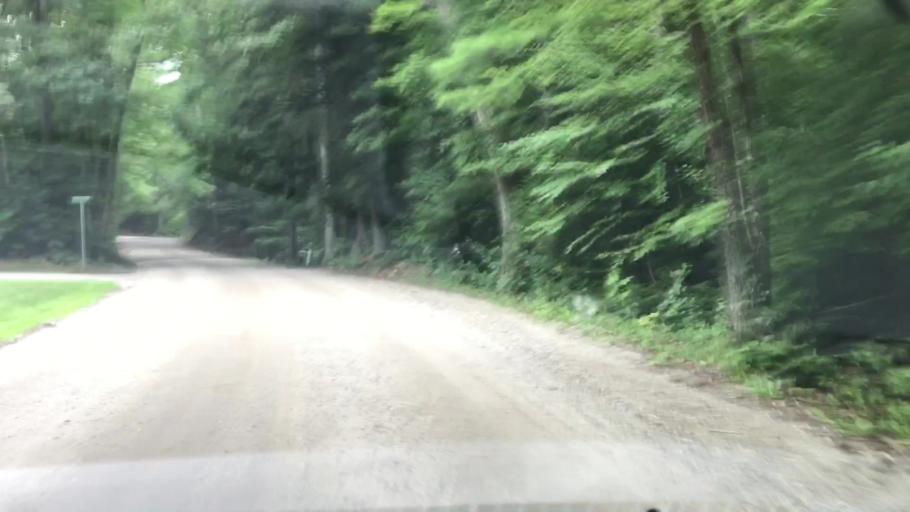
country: US
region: New Hampshire
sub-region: Hillsborough County
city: Milford
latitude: 42.8799
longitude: -71.6165
